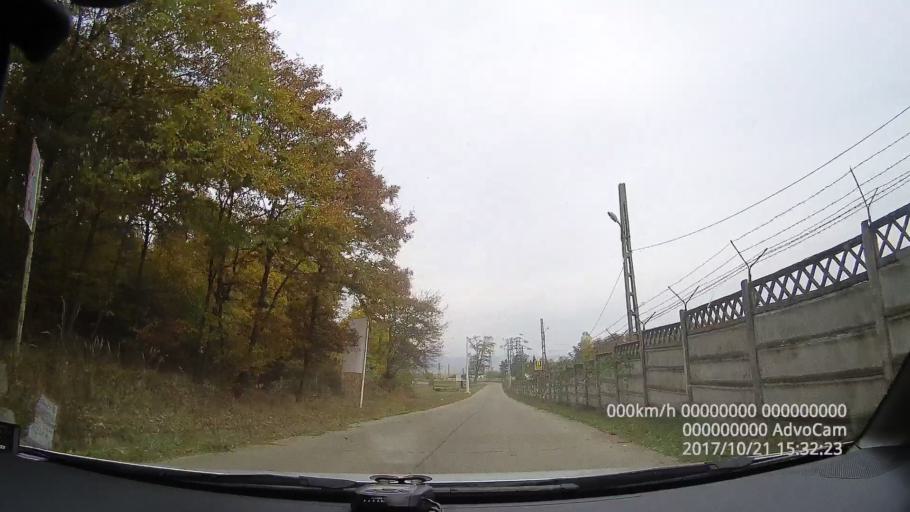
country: RO
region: Hunedoara
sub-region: Comuna Soimus
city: Soimus
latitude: 45.9013
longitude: 22.8869
